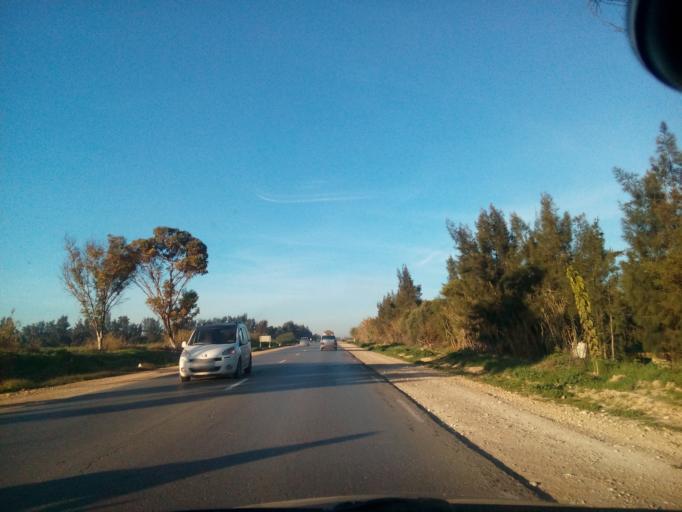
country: DZ
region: Relizane
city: Relizane
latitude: 35.7315
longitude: 0.4384
